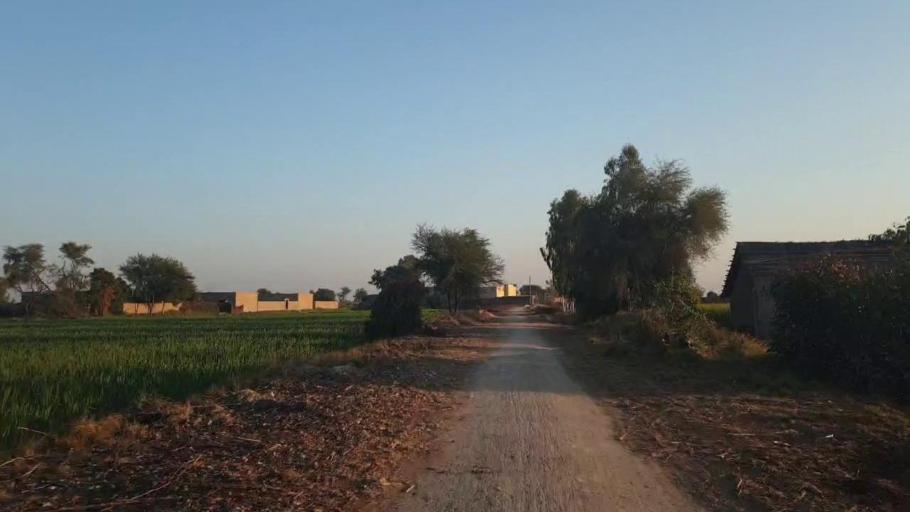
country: PK
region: Sindh
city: Khadro
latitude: 26.0753
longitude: 68.7005
